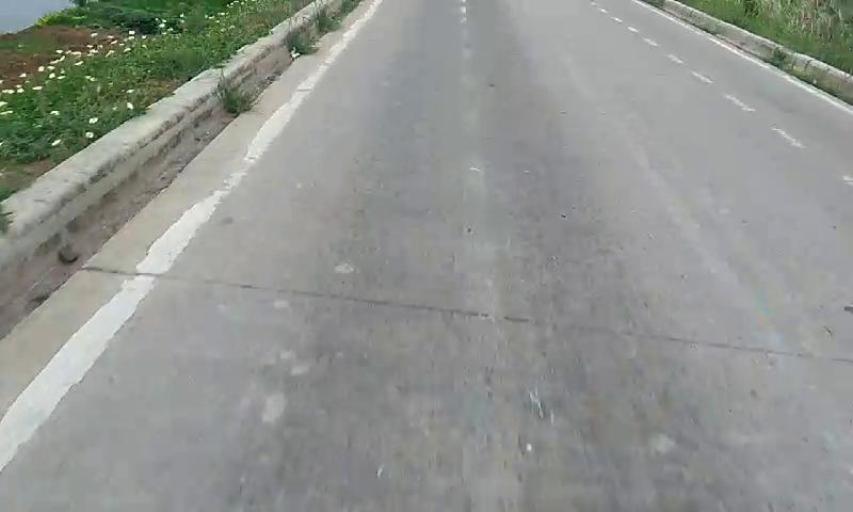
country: ID
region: West Java
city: Bekasi
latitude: -6.1462
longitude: 106.9702
